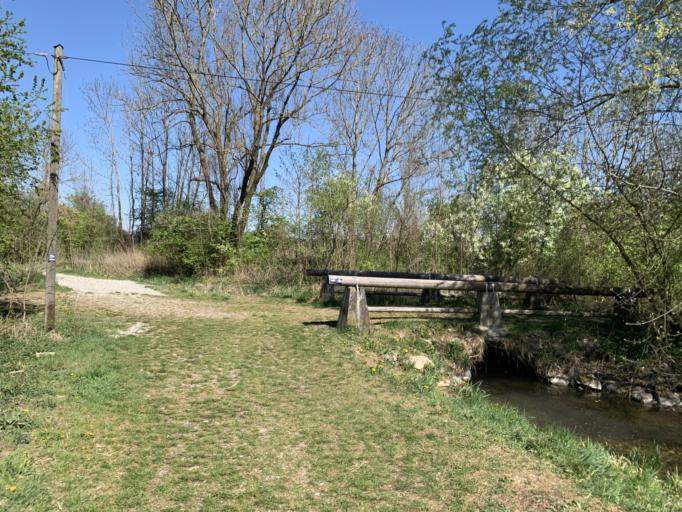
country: DE
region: Bavaria
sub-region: Swabia
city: Gersthofen
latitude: 48.4393
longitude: 10.8918
